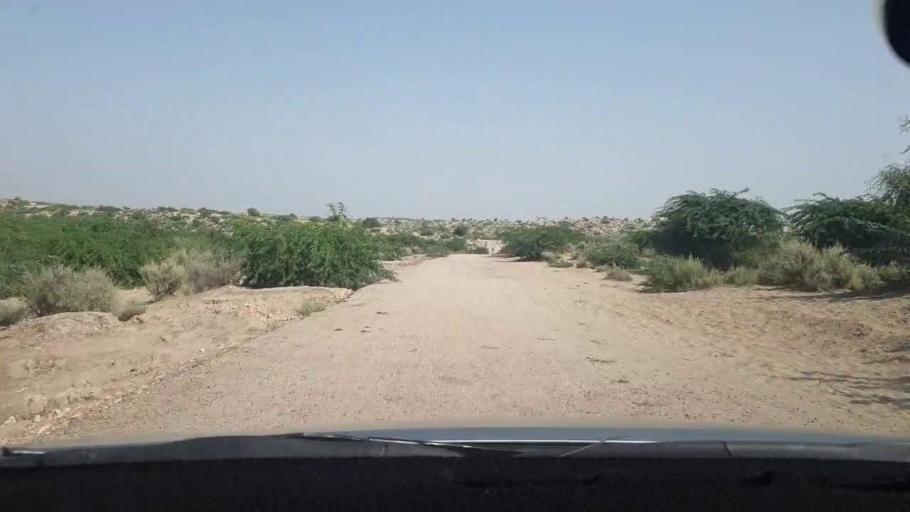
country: PK
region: Sindh
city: Pithoro
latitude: 25.7804
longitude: 69.4831
